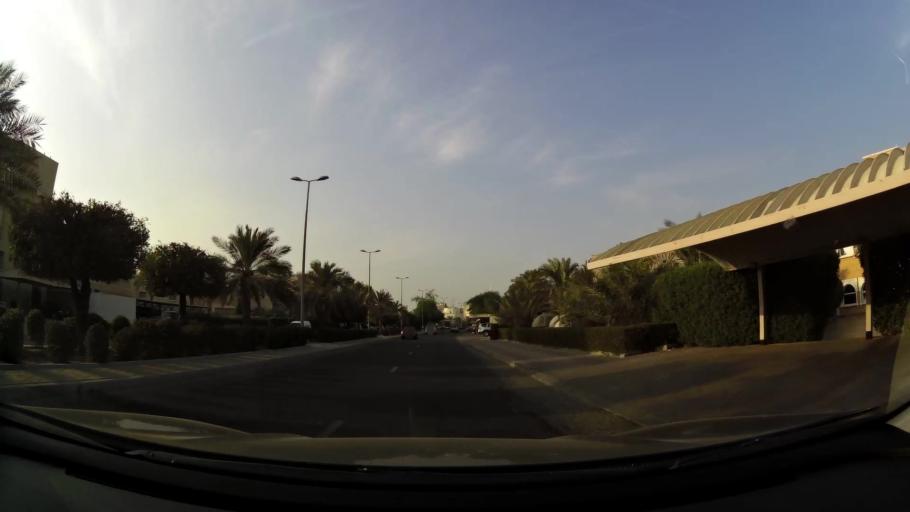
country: KW
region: Mubarak al Kabir
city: Sabah as Salim
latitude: 29.2558
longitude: 48.0704
